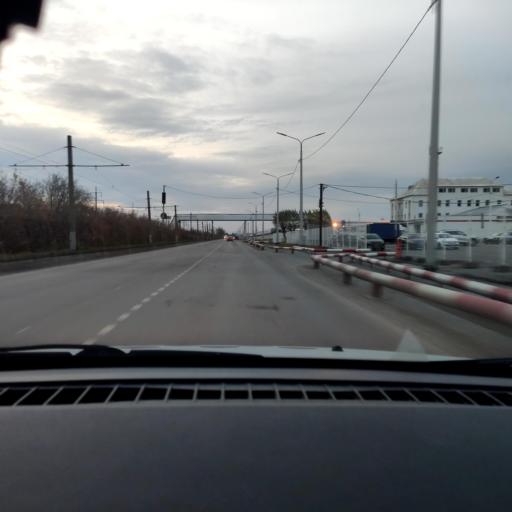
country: RU
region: Perm
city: Gamovo
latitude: 57.9224
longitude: 56.1418
